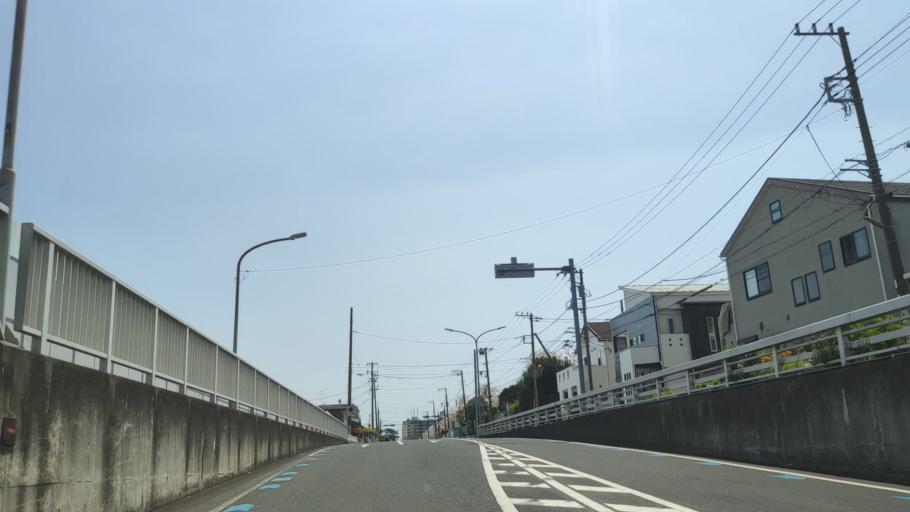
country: JP
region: Kanagawa
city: Hiratsuka
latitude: 35.3241
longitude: 139.3380
